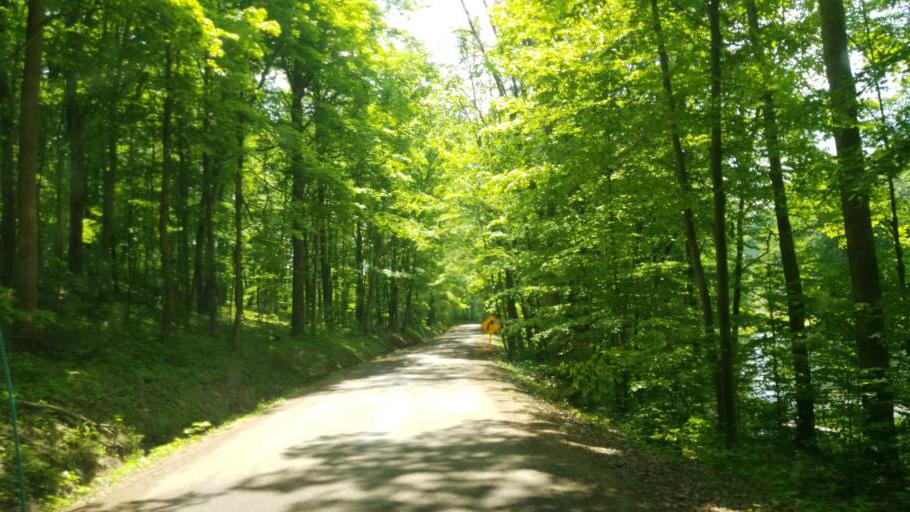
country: US
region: Ohio
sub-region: Sandusky County
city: Bellville
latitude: 40.6652
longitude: -82.3903
